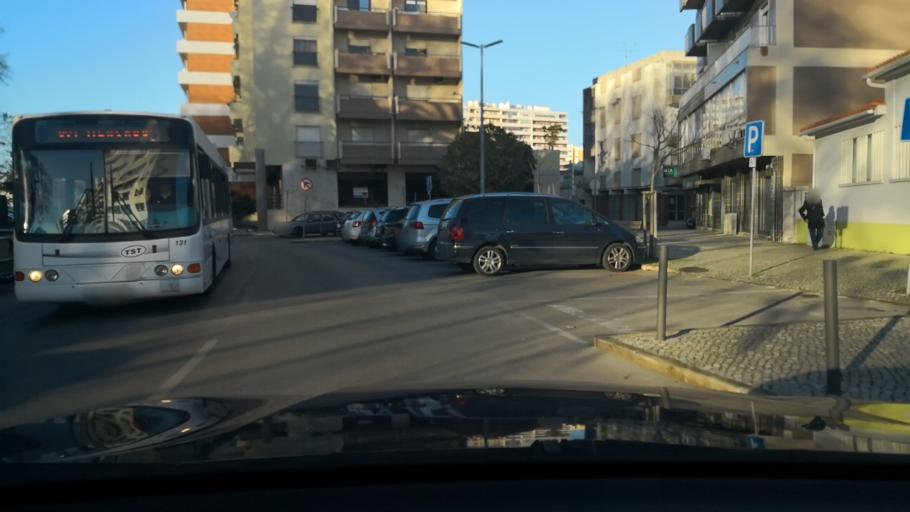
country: PT
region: Setubal
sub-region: Setubal
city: Setubal
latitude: 38.5279
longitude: -8.8898
